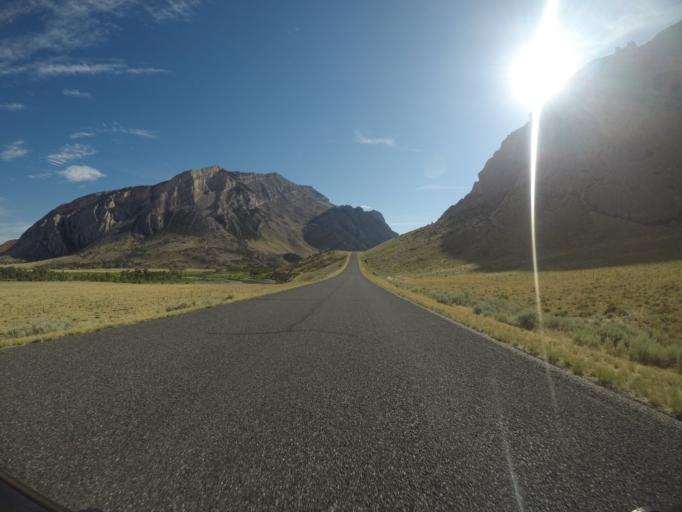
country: US
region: Montana
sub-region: Carbon County
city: Red Lodge
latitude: 44.8564
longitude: -109.2942
